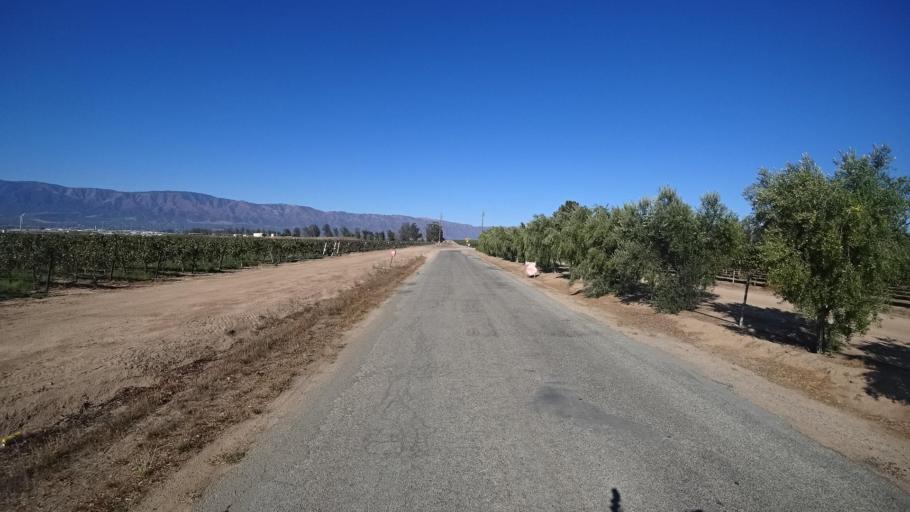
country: US
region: California
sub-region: Monterey County
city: Soledad
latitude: 36.4886
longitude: -121.3637
